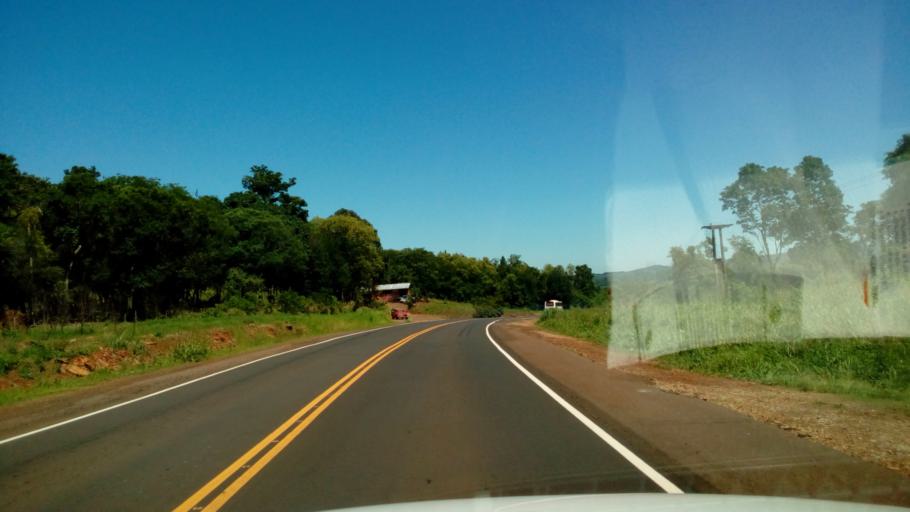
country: AR
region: Misiones
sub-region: Departamento de Leandro N. Alem
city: Leandro N. Alem
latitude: -27.5879
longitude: -55.3631
